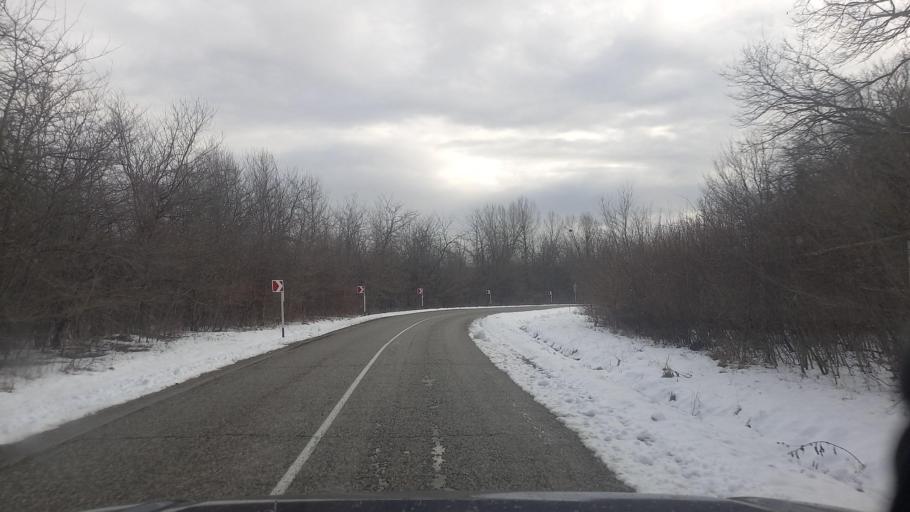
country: RU
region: Krasnodarskiy
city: Smolenskaya
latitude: 44.7689
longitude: 38.8466
